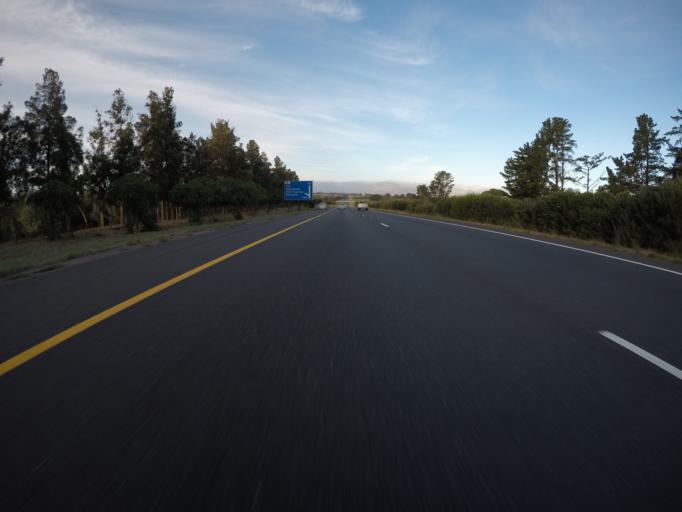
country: ZA
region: Western Cape
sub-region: Cape Winelands District Municipality
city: Stellenbosch
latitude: -33.8038
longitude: 18.8487
